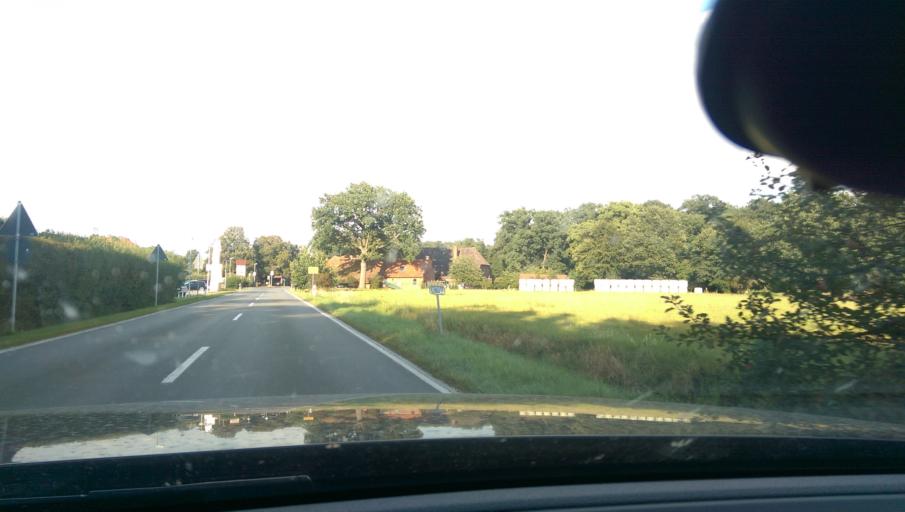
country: DE
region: Lower Saxony
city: Schwarmstedt
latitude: 52.5727
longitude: 9.5615
